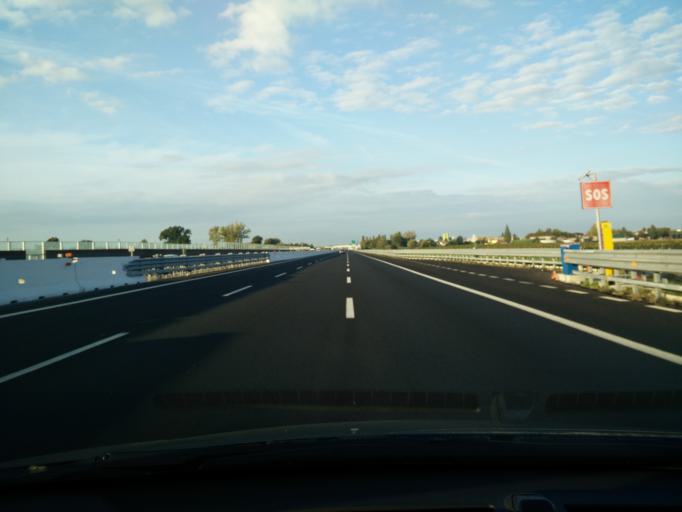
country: IT
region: Veneto
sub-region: Provincia di Venezia
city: Meolo
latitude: 45.6372
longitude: 12.4578
